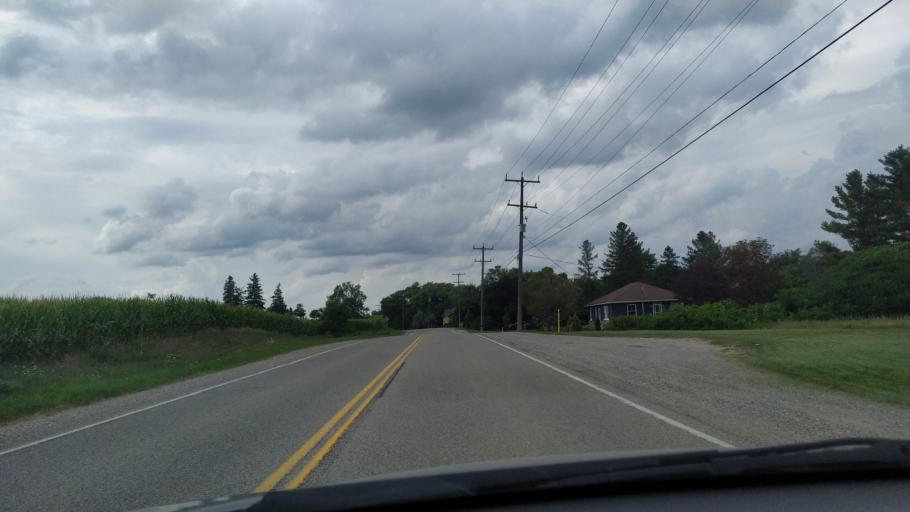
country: CA
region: Ontario
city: Kitchener
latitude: 43.3552
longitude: -80.5429
